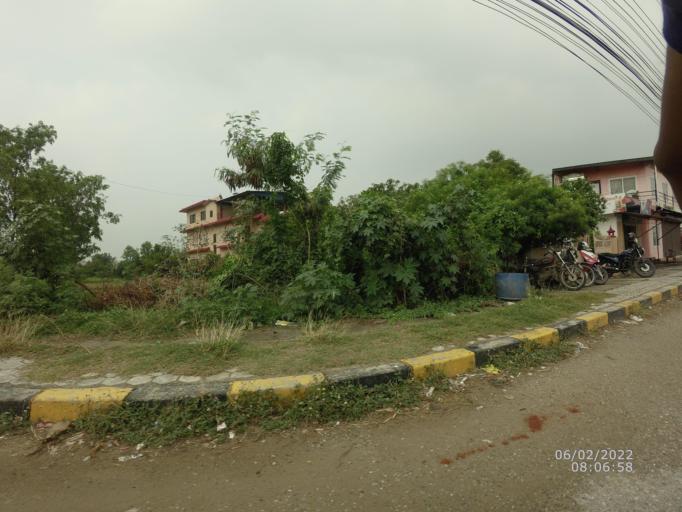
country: NP
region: Western Region
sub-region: Lumbini Zone
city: Bhairahawa
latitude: 27.4815
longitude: 83.4648
